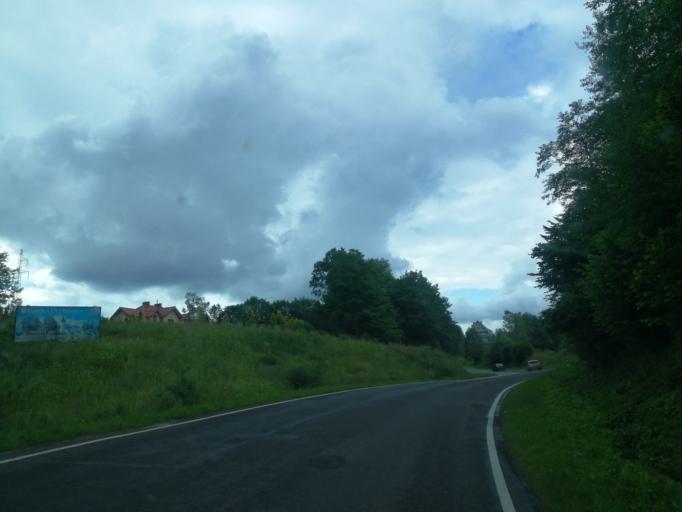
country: PL
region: Subcarpathian Voivodeship
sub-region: Powiat leski
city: Olszanica
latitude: 49.4305
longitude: 22.4562
